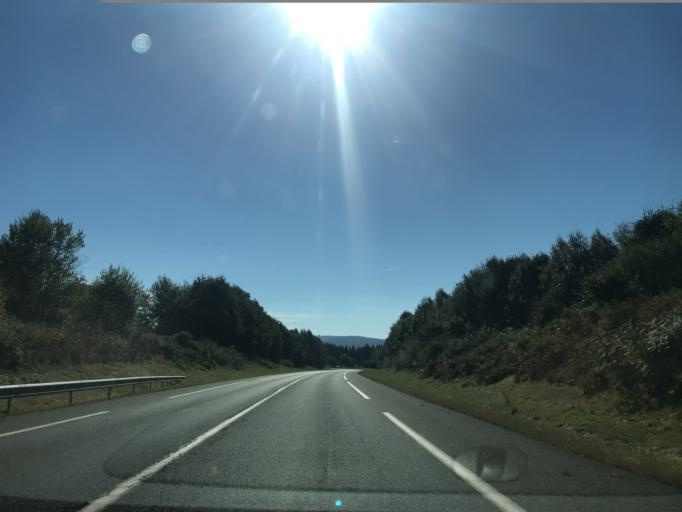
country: FR
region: Auvergne
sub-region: Departement du Puy-de-Dome
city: Saint-Sauves-d'Auvergne
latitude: 45.6597
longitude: 2.6870
